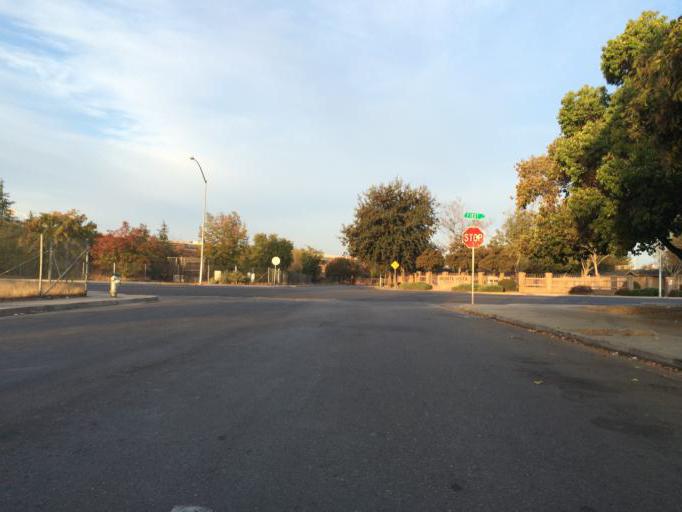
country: US
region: California
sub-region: Fresno County
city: Fresno
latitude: 36.7559
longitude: -119.7721
